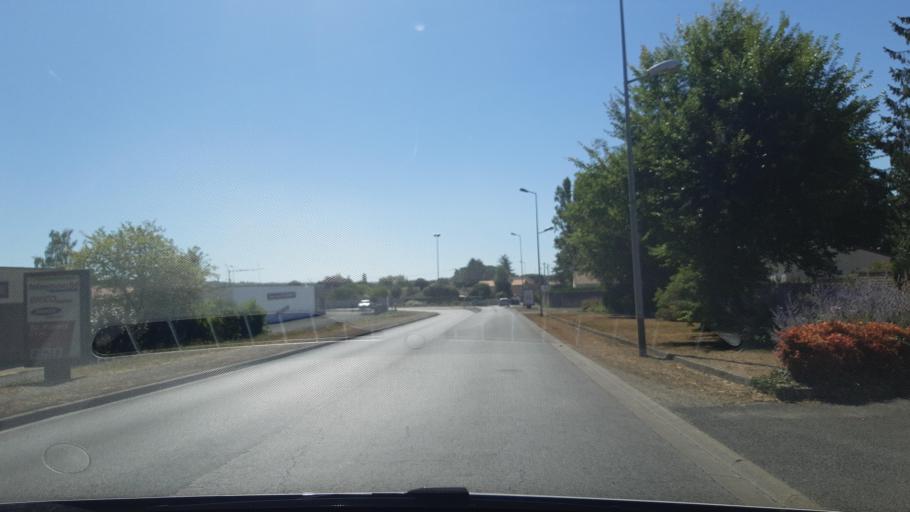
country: FR
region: Poitou-Charentes
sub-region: Departement des Deux-Sevres
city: Exireuil
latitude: 46.4195
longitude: -0.2055
